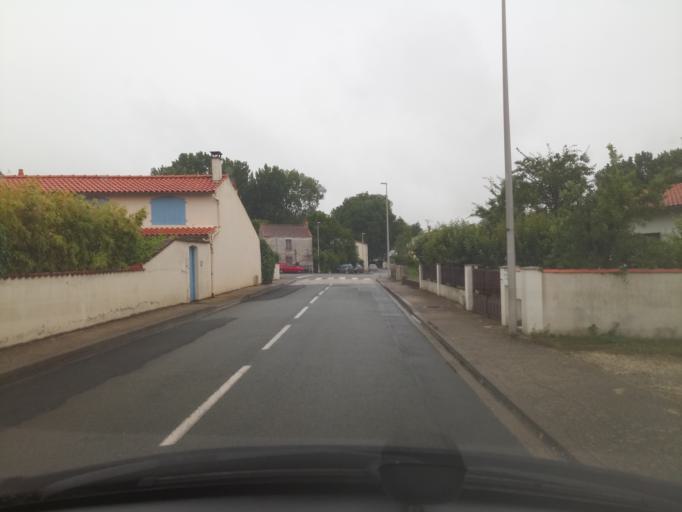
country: FR
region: Poitou-Charentes
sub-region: Departement de la Charente-Maritime
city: Andilly
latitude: 46.2291
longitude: -0.9931
